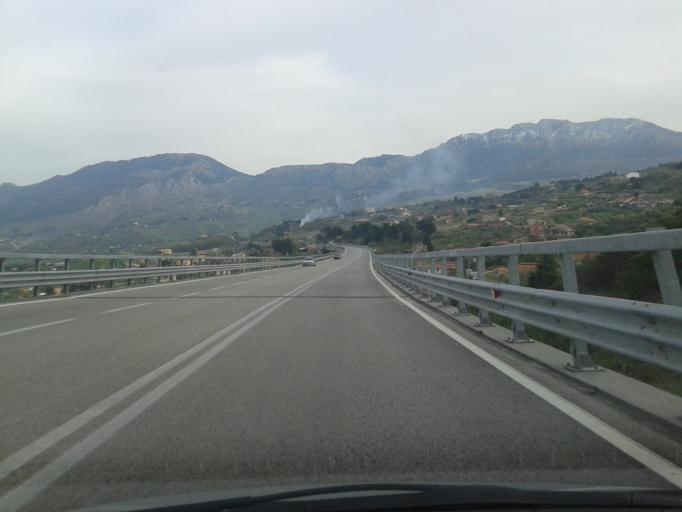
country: IT
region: Sicily
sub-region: Palermo
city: Giacalone
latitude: 38.0378
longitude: 13.2396
